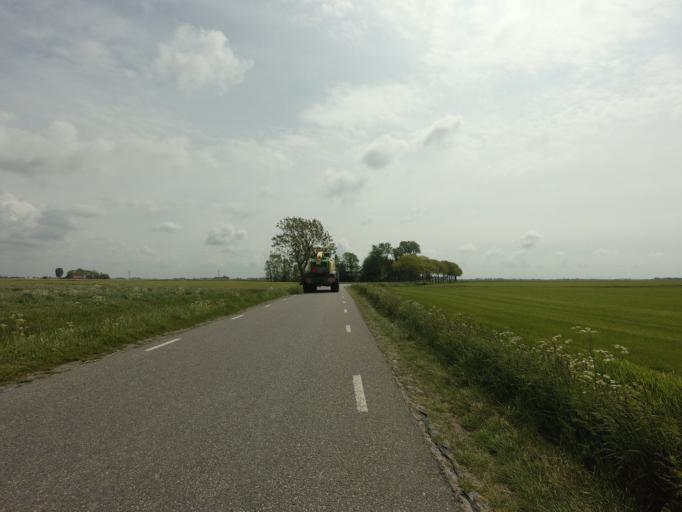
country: NL
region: Friesland
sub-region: Sudwest Fryslan
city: Bolsward
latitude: 53.1110
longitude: 5.4906
